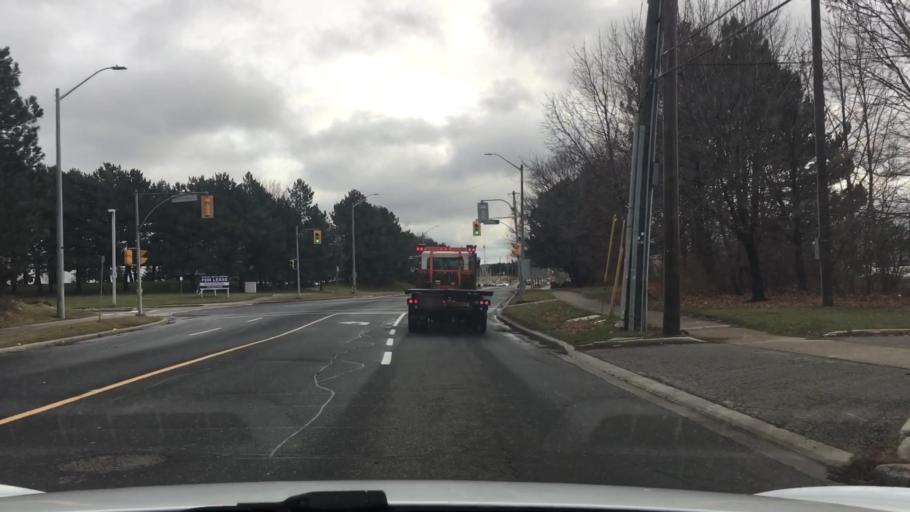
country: CA
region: Ontario
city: Willowdale
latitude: 43.8190
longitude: -79.3430
